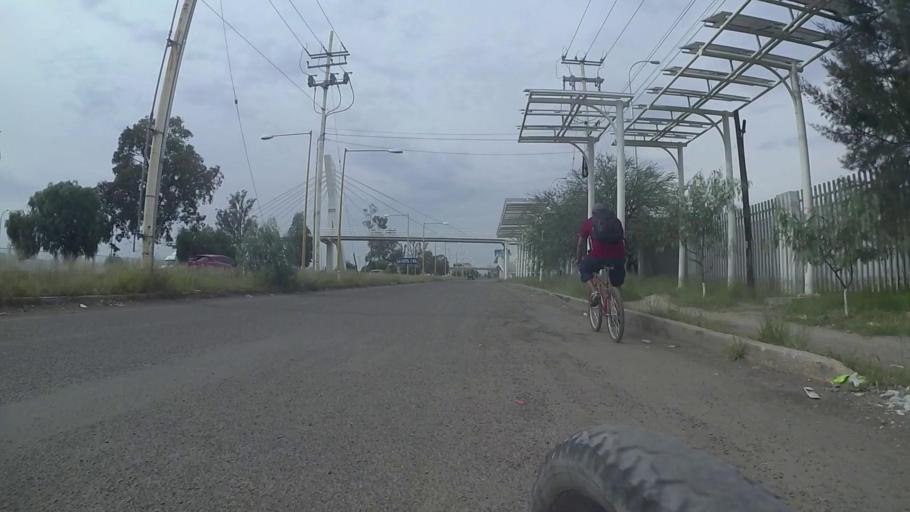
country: MX
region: Aguascalientes
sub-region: Aguascalientes
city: Penuelas (El Cienegal)
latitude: 21.7377
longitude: -102.2767
